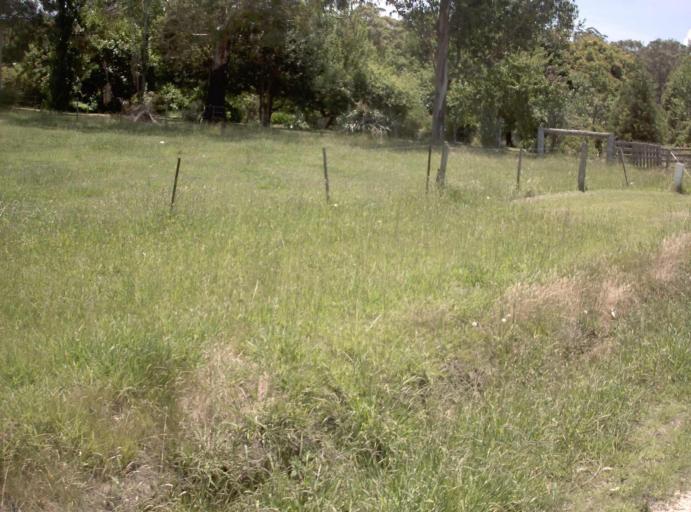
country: AU
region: New South Wales
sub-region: Bombala
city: Bombala
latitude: -37.5121
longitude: 148.9292
